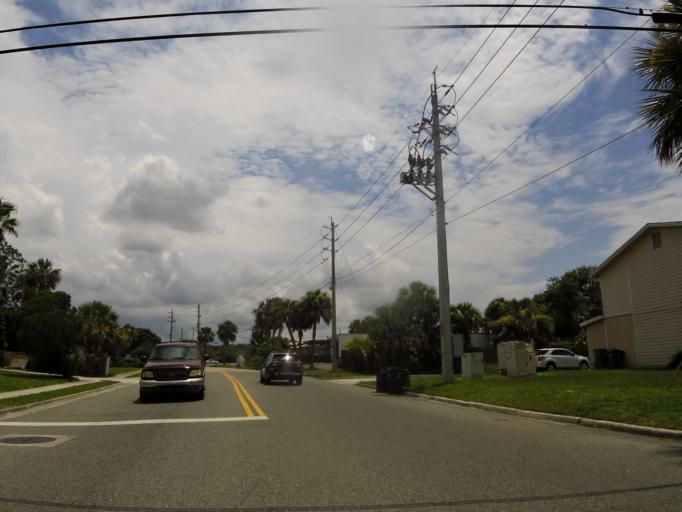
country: US
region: Florida
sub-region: Duval County
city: Atlantic Beach
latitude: 30.3270
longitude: -81.4104
